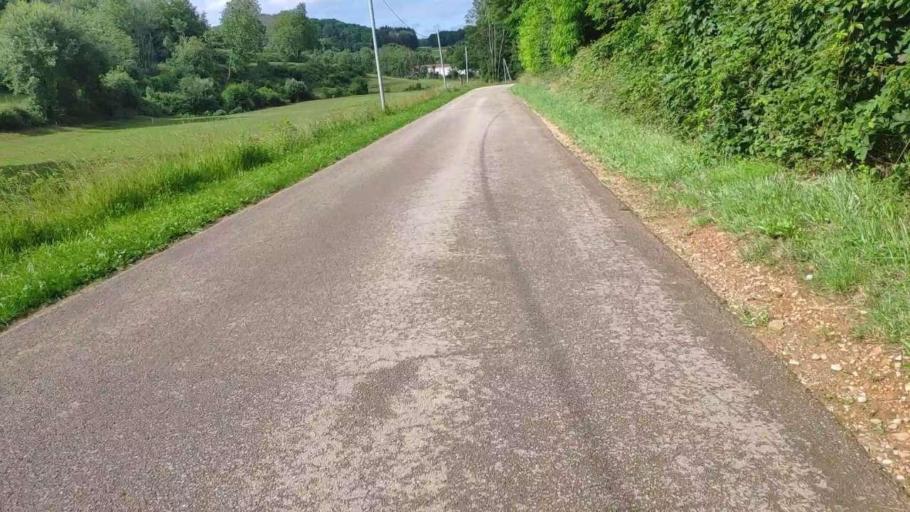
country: FR
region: Franche-Comte
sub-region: Departement du Jura
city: Poligny
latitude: 46.8307
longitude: 5.5755
